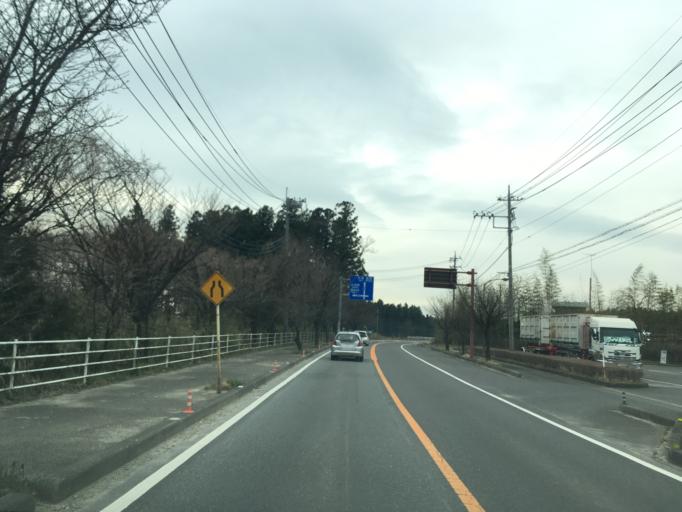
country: JP
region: Tochigi
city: Kuroiso
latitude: 36.9734
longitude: 139.9274
